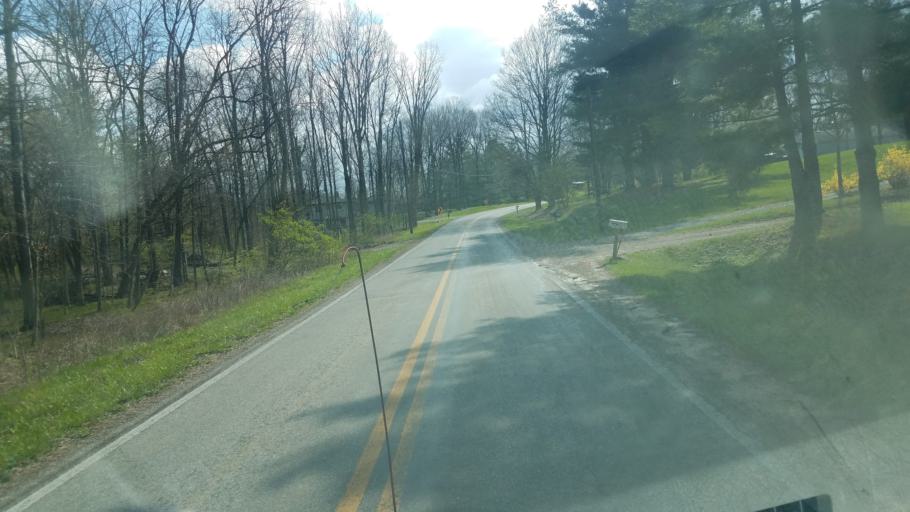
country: US
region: Ohio
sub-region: Delaware County
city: Delaware
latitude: 40.3658
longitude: -83.0280
